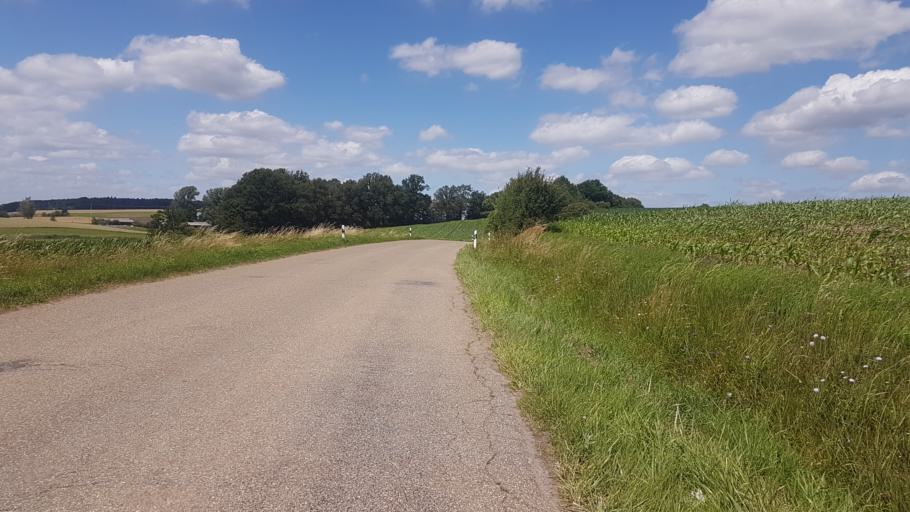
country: DE
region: Bavaria
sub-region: Regierungsbezirk Mittelfranken
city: Colmberg
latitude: 49.3315
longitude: 10.3756
